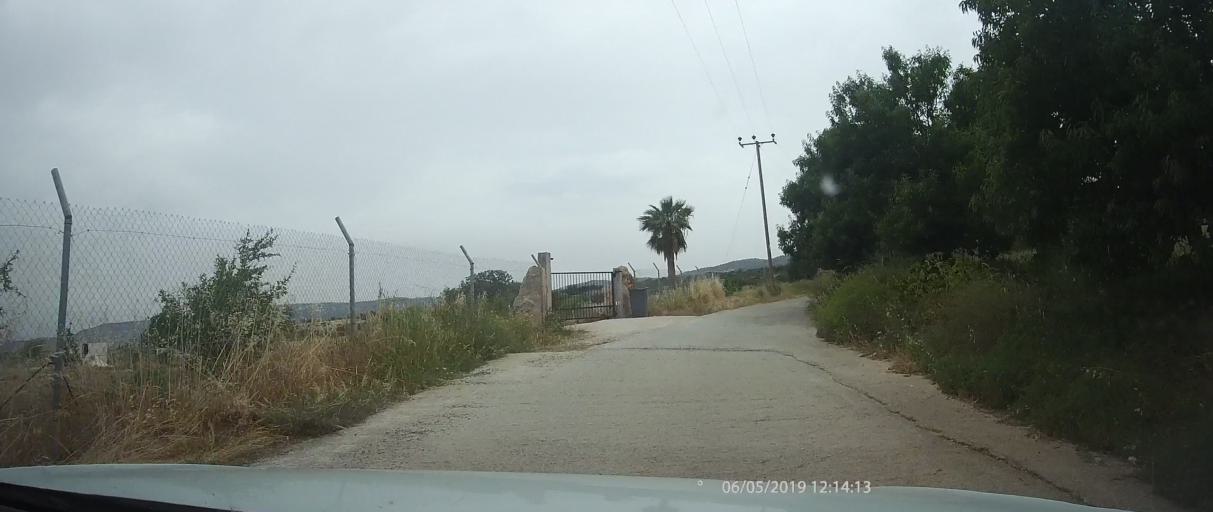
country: CY
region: Pafos
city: Tala
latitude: 34.8452
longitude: 32.4215
